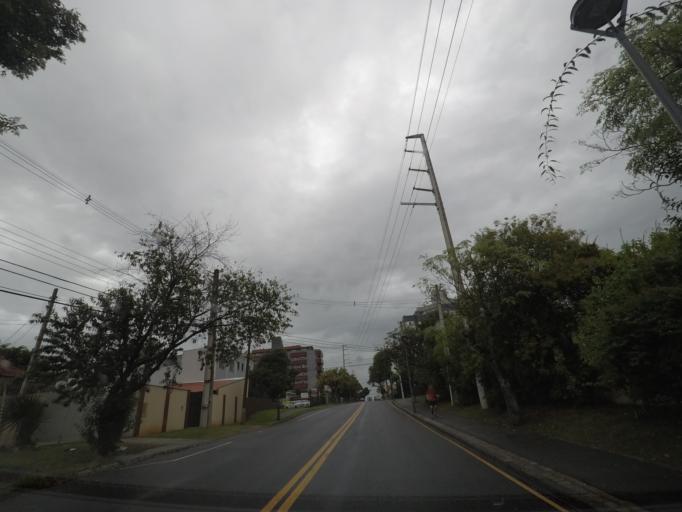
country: BR
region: Parana
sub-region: Curitiba
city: Curitiba
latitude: -25.4575
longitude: -49.2825
